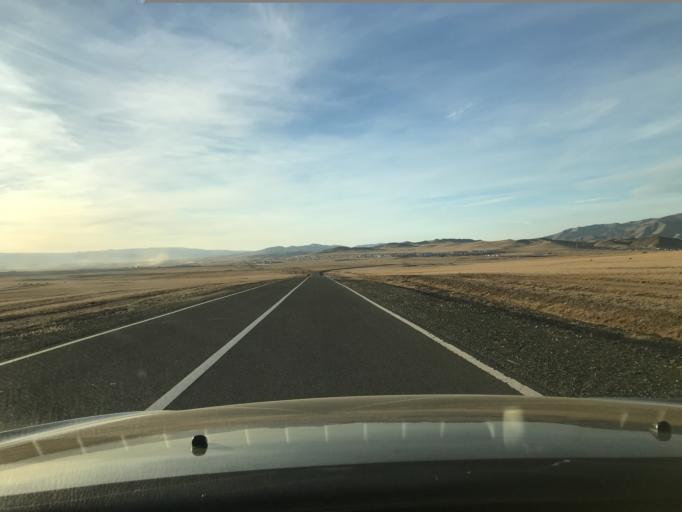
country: MN
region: Central Aimak
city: Arhust
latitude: 47.7640
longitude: 107.4318
